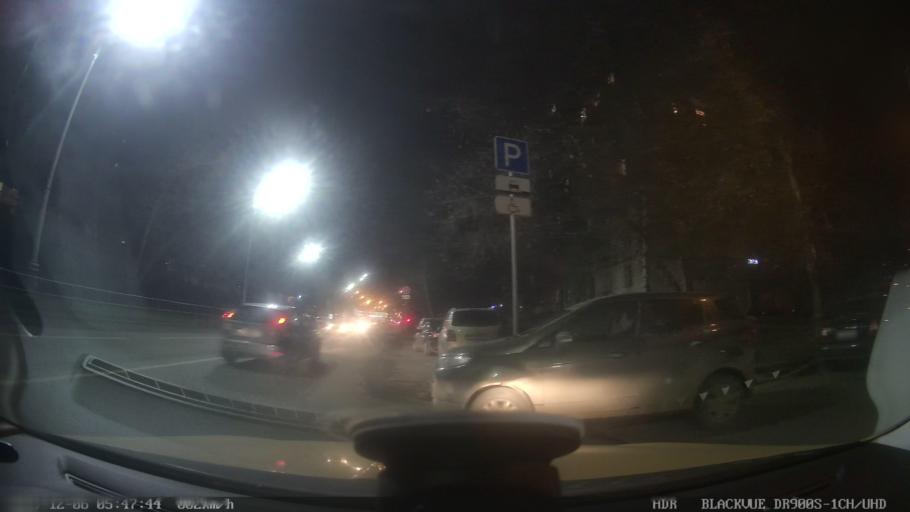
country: RU
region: Moscow
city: Vatutino
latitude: 55.8843
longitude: 37.6619
